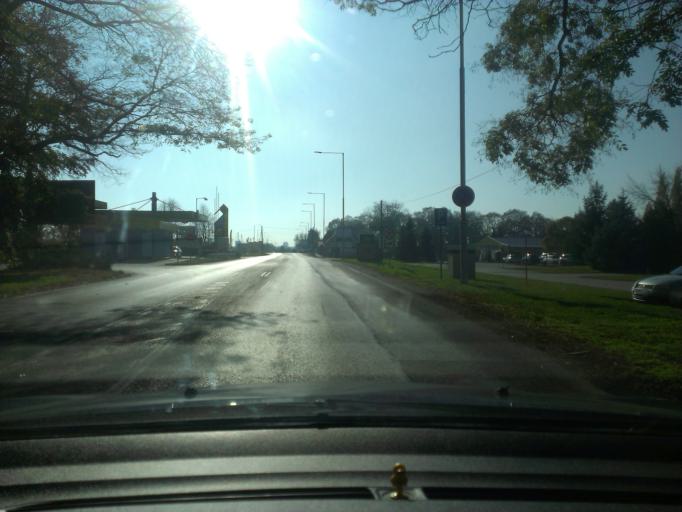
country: SK
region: Nitriansky
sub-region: Okres Nove Zamky
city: Nove Zamky
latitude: 48.0099
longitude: 18.1559
